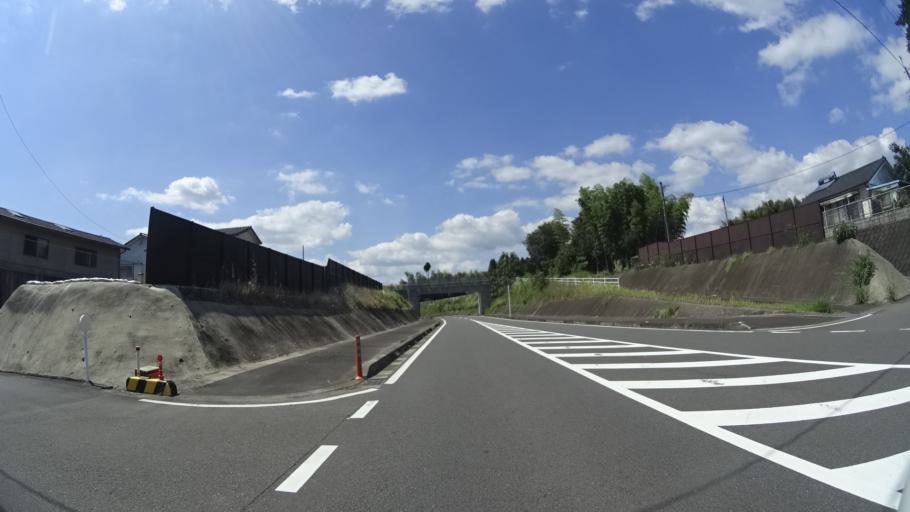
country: JP
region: Kagoshima
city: Kajiki
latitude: 31.8150
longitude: 130.7020
